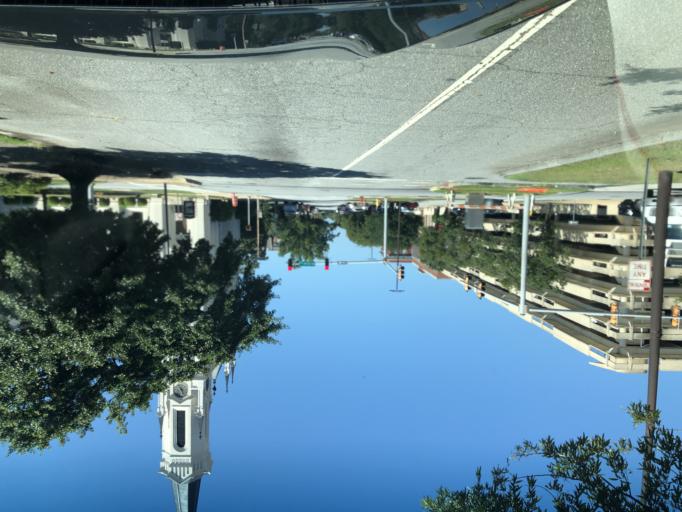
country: US
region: Georgia
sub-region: Muscogee County
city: Columbus
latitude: 32.4664
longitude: -84.9917
